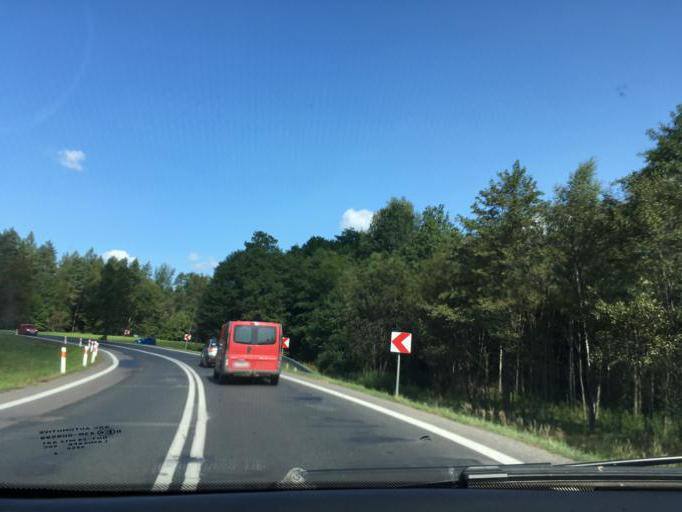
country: PL
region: Subcarpathian Voivodeship
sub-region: Powiat sanocki
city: Zagorz
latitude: 49.5090
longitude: 22.2934
